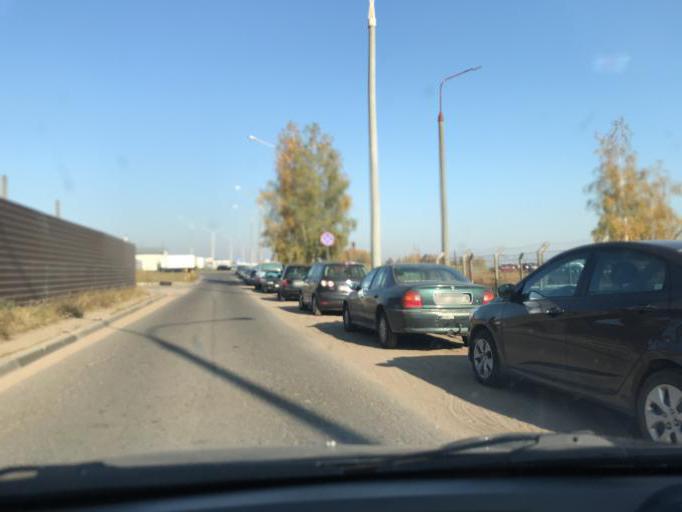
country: BY
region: Minsk
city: Pryvol'ny
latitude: 53.8130
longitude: 27.7858
